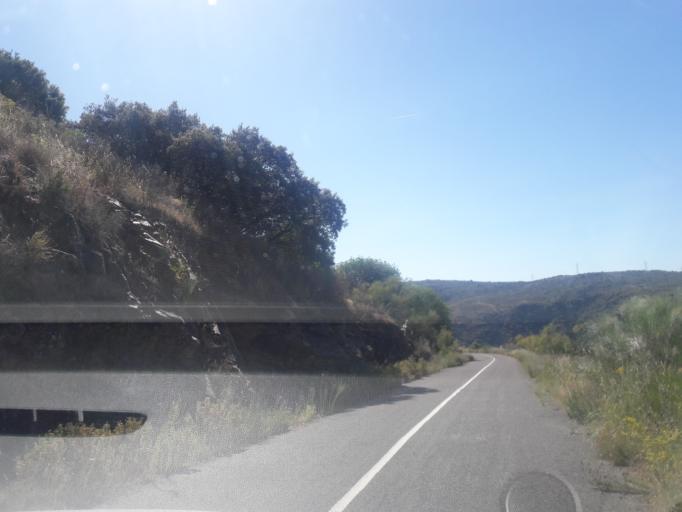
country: ES
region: Castille and Leon
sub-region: Provincia de Salamanca
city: Saucelle
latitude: 41.0348
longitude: -6.7489
